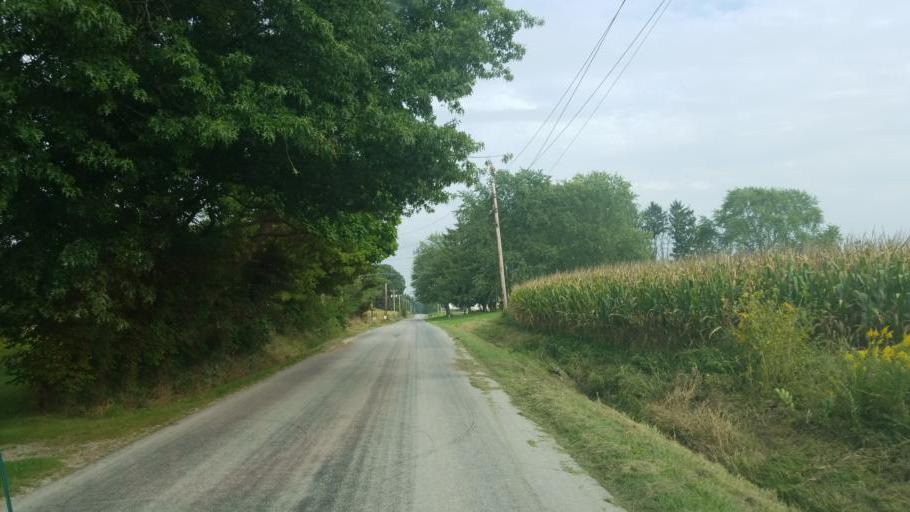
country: US
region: Ohio
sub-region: Wayne County
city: West Salem
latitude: 40.9910
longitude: -82.0682
